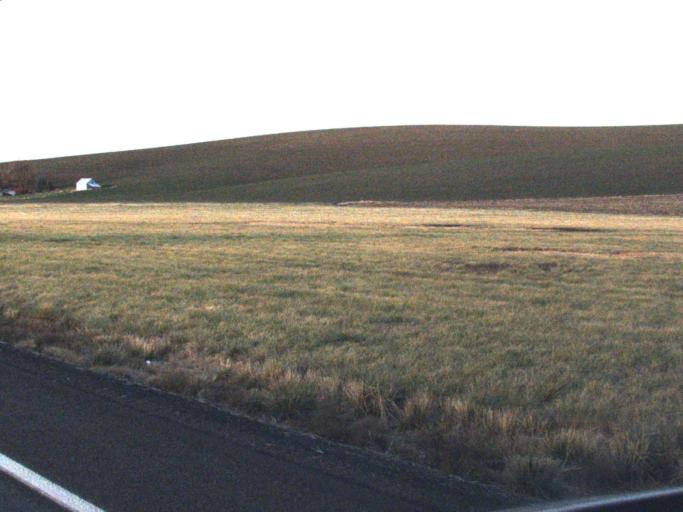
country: US
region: Washington
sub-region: Whitman County
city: Colfax
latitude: 46.7984
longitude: -117.6708
